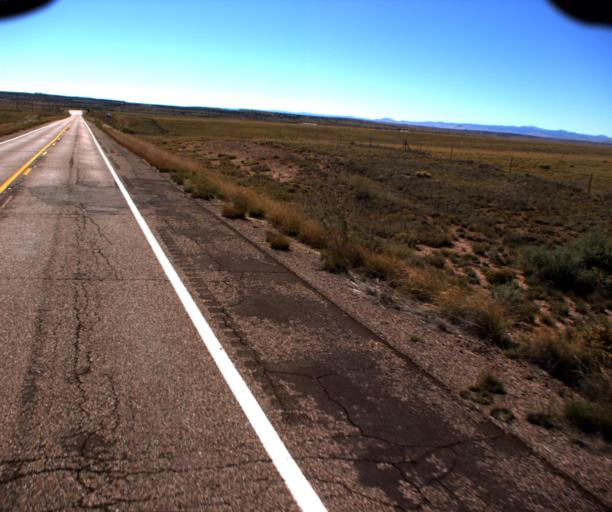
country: US
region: Arizona
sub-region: Apache County
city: Saint Johns
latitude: 34.5188
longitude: -109.4522
